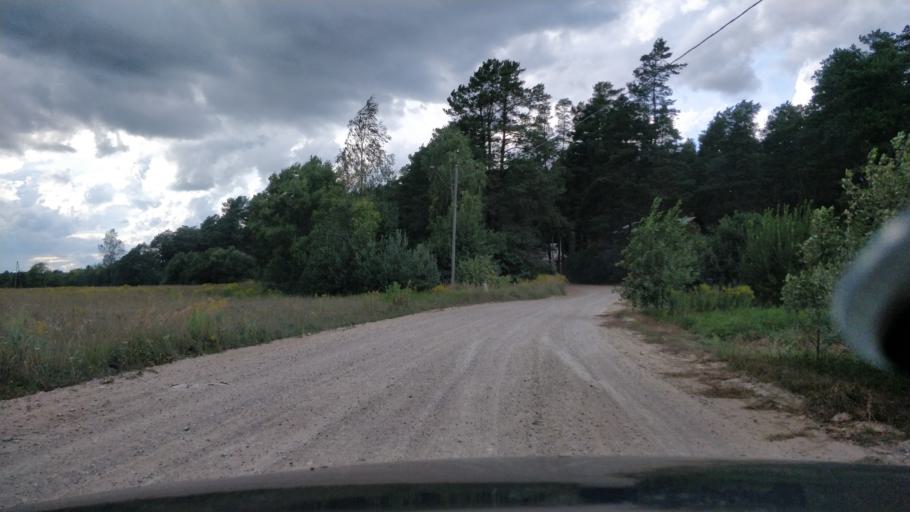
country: LV
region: Ogre
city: Ogre
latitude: 56.7953
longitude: 24.6466
